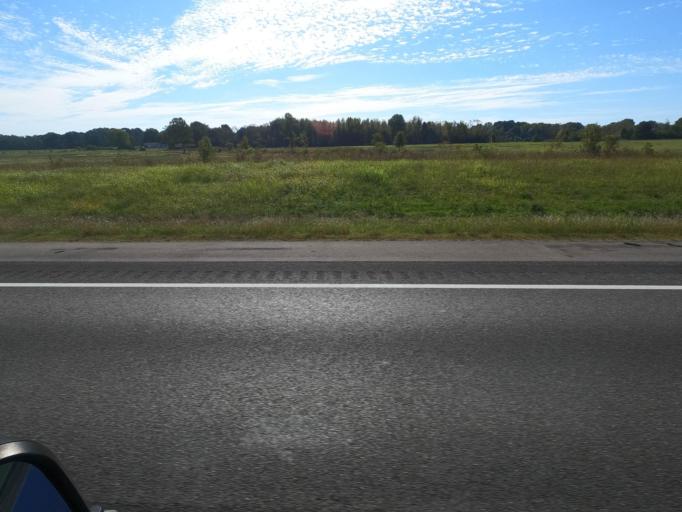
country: US
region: Tennessee
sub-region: Tipton County
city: Mason
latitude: 35.3798
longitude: -89.4428
